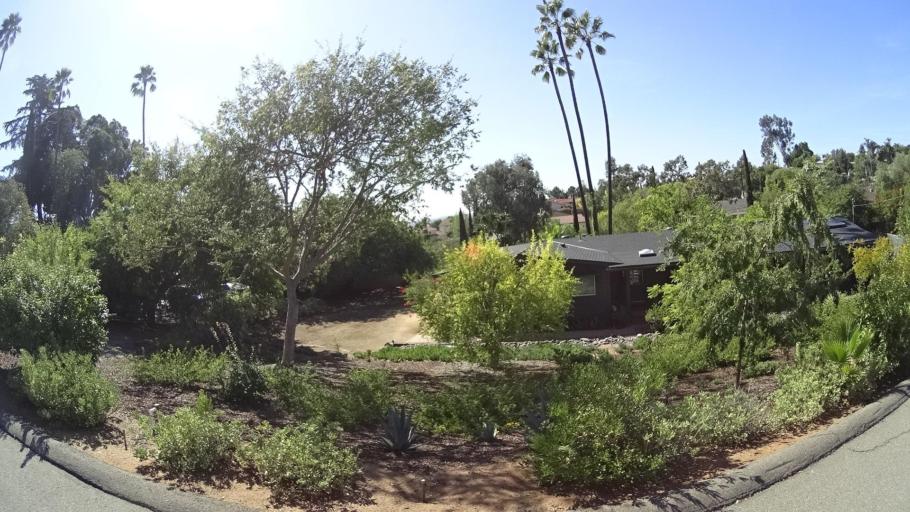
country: US
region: California
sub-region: San Diego County
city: Casa de Oro-Mount Helix
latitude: 32.7562
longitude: -116.9744
